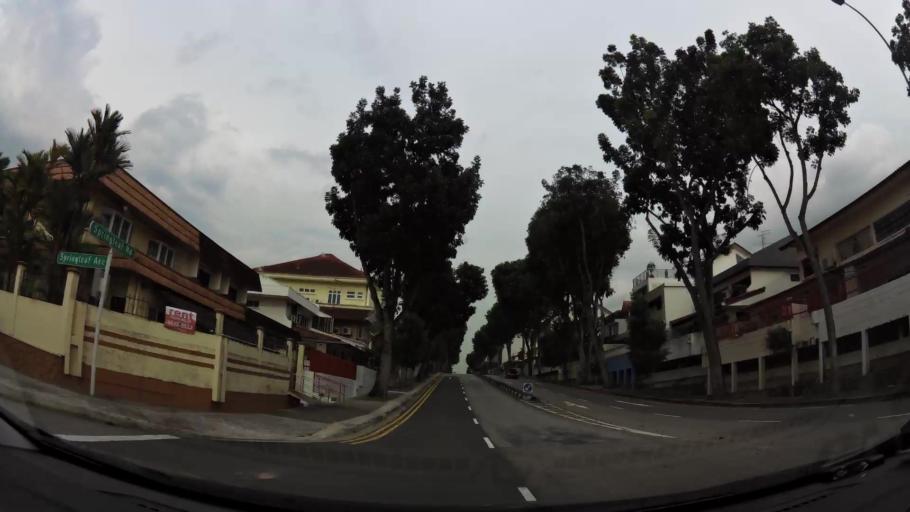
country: MY
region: Johor
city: Johor Bahru
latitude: 1.3971
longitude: 103.8201
